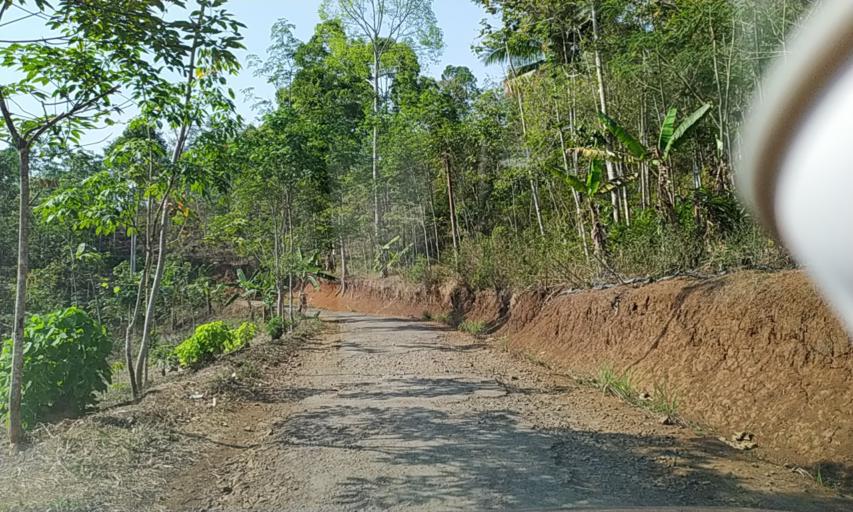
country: ID
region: Central Java
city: Datar
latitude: -7.2188
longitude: 108.6213
